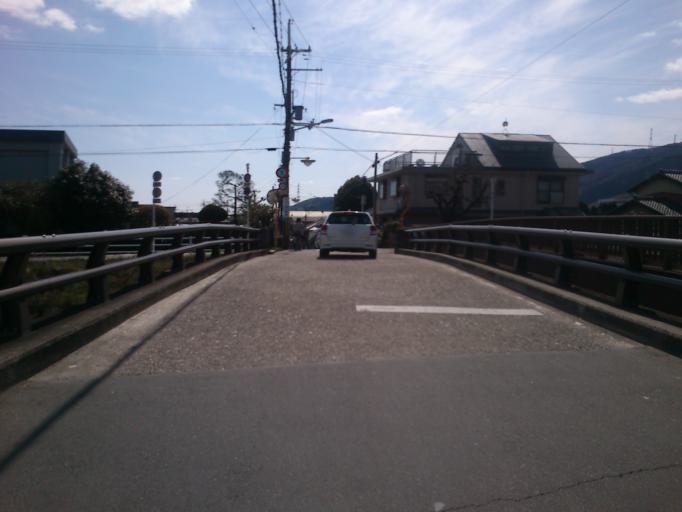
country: JP
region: Kyoto
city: Yawata
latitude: 34.8877
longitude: 135.6715
